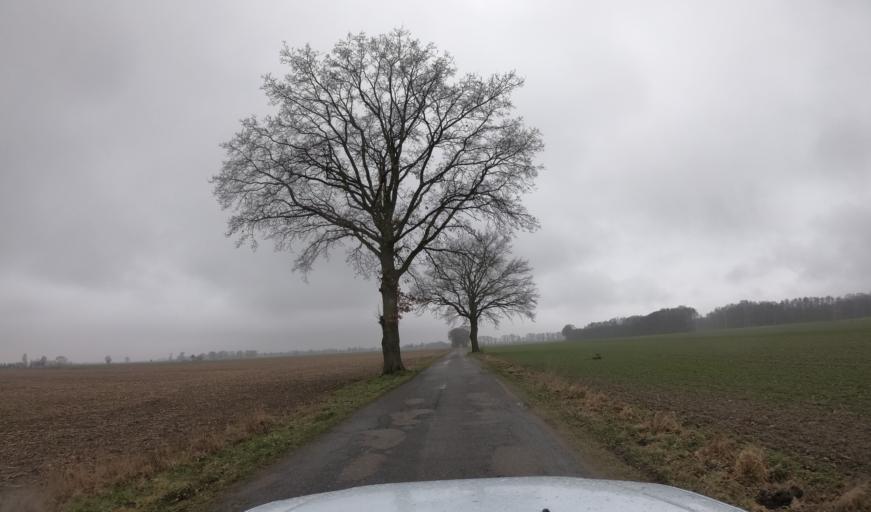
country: PL
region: West Pomeranian Voivodeship
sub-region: Powiat kamienski
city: Kamien Pomorski
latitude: 53.9039
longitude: 14.8211
